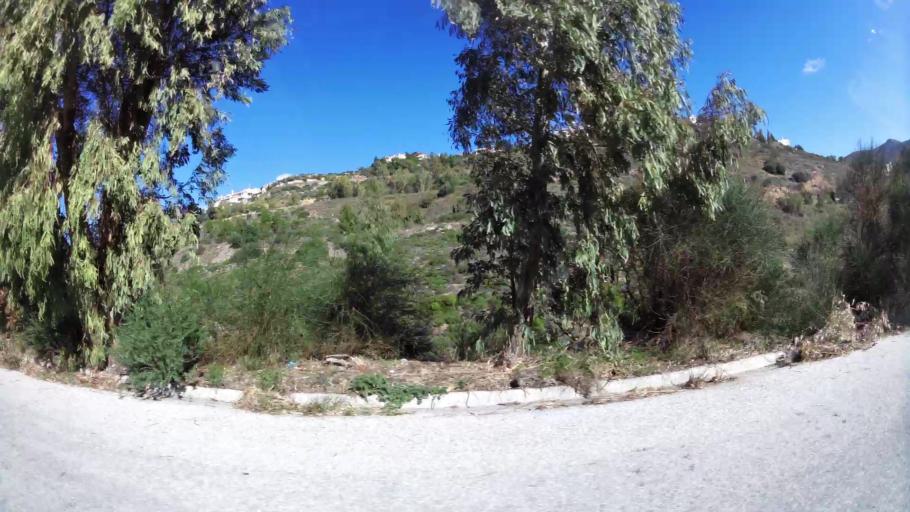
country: GR
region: Attica
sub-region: Nomarchia Anatolikis Attikis
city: Dhrafi
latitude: 38.0395
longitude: 23.9005
